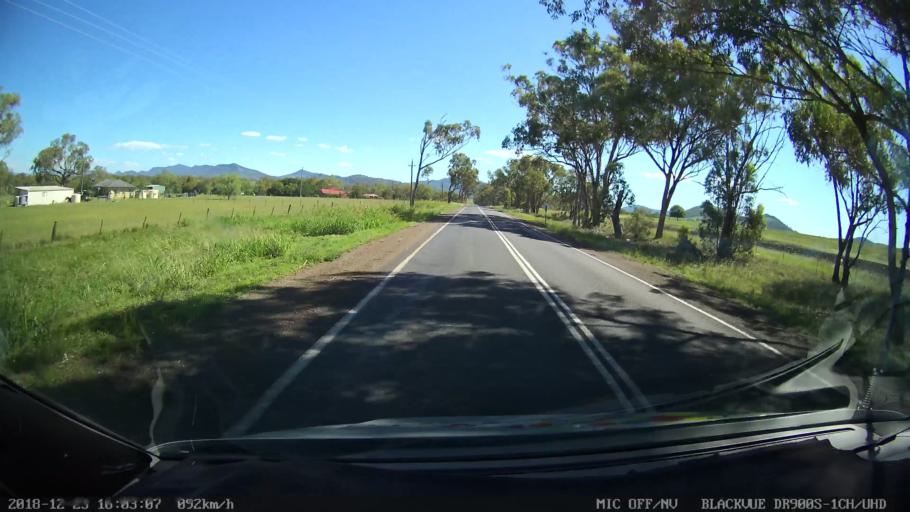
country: AU
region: New South Wales
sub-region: Tamworth Municipality
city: Phillip
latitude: -31.2399
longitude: 150.8034
